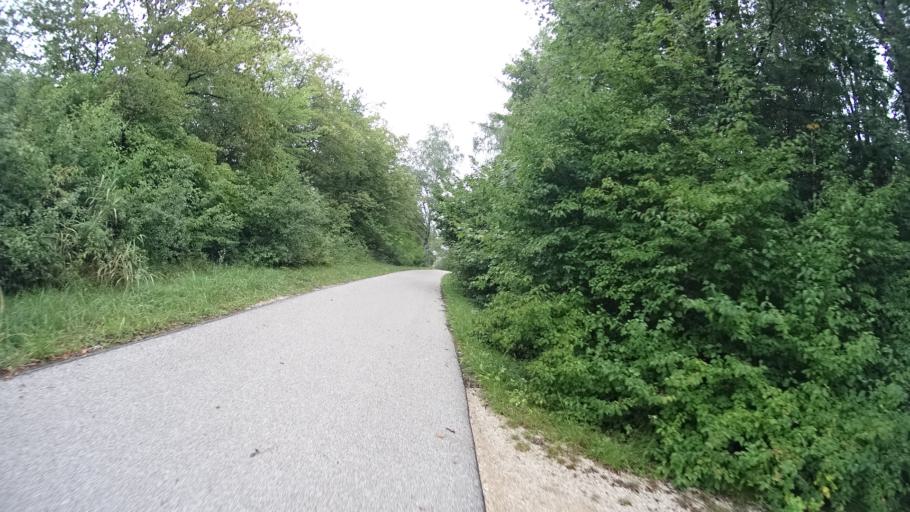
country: DE
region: Bavaria
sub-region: Upper Bavaria
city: Denkendorf
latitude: 48.9165
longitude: 11.4563
